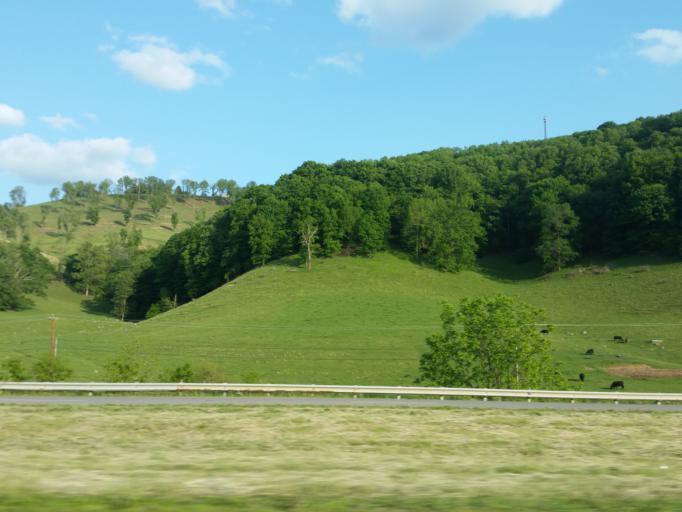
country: US
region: Virginia
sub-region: Russell County
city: Honaker
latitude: 36.9520
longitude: -81.9487
